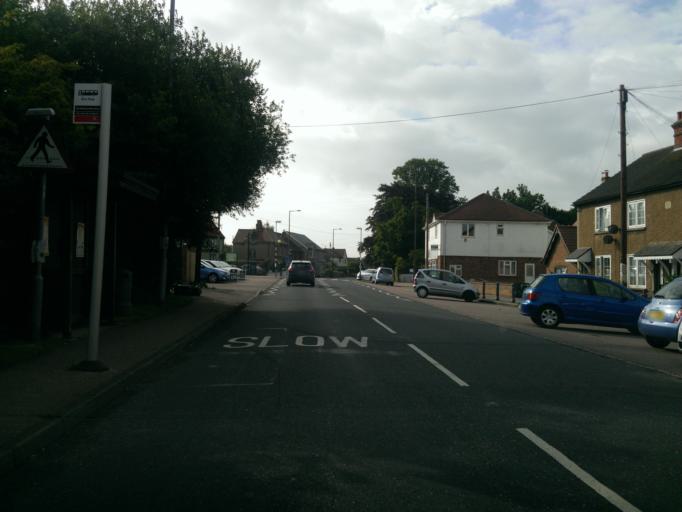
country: GB
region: England
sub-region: Essex
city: Little Clacton
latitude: 51.8273
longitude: 1.1419
